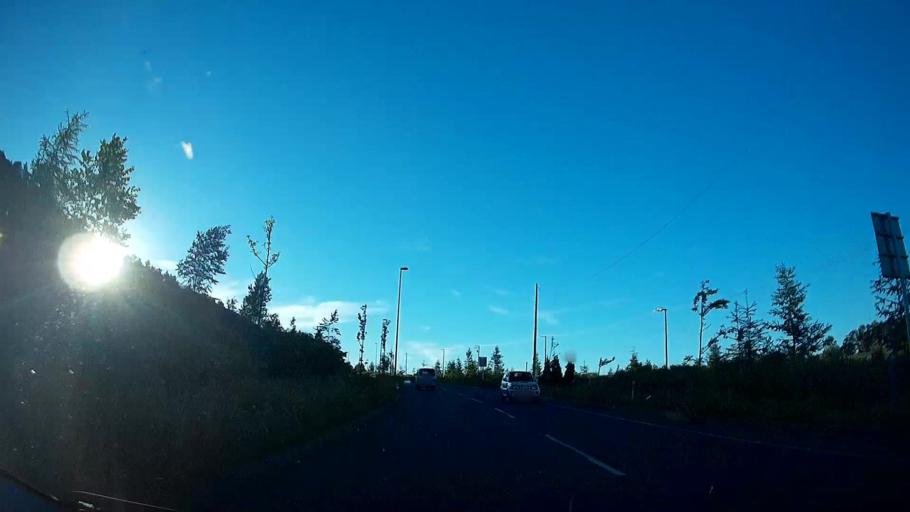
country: JP
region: Hokkaido
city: Otaru
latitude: 43.1657
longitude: 141.0234
